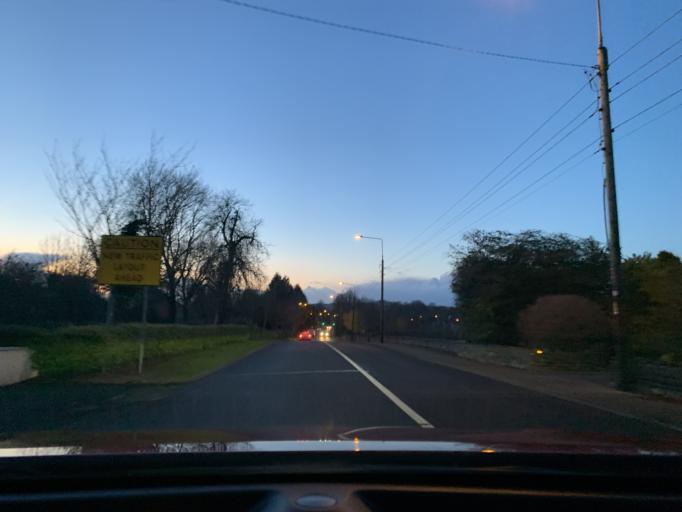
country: IE
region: Connaught
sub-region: Roscommon
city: Boyle
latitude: 53.9713
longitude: -8.2889
